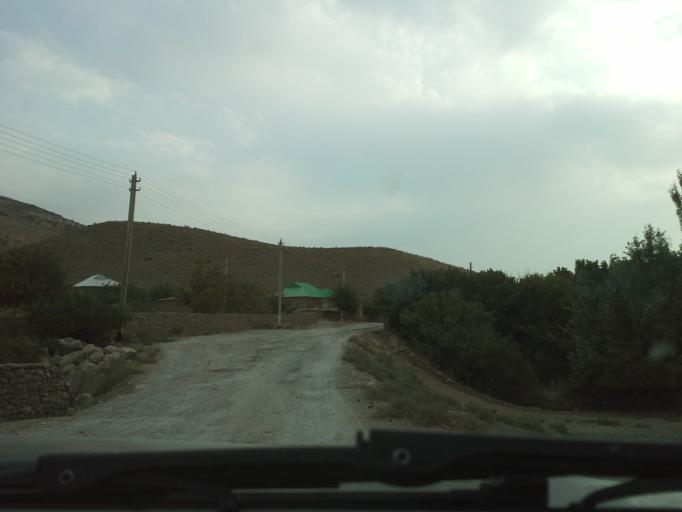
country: UZ
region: Qashqadaryo
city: Qorashina
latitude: 37.9249
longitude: 66.4920
